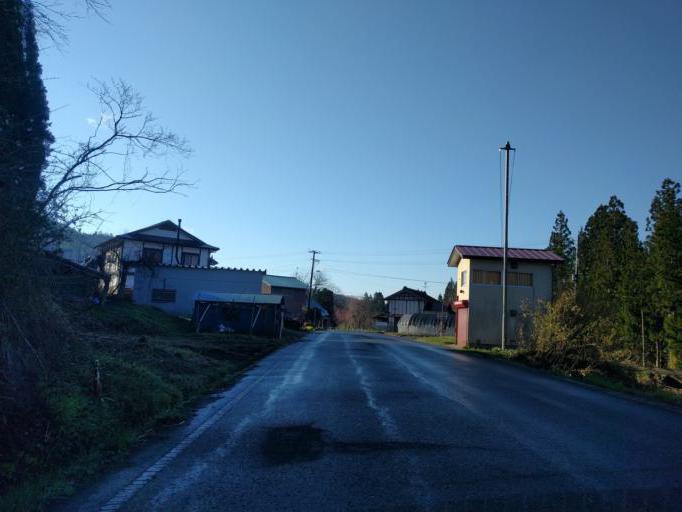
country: JP
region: Fukushima
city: Kitakata
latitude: 37.7073
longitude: 139.7830
